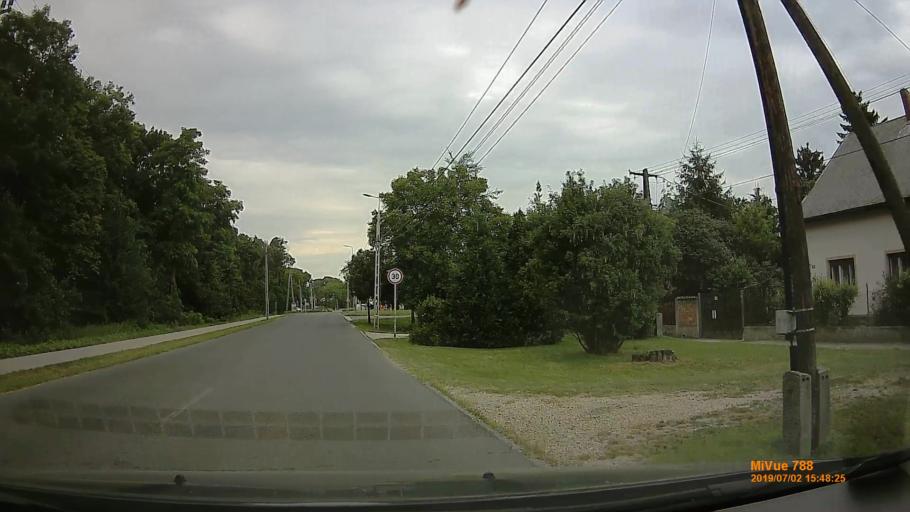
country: HU
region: Gyor-Moson-Sopron
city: Mosonmagyarovar
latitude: 47.8778
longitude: 17.2820
